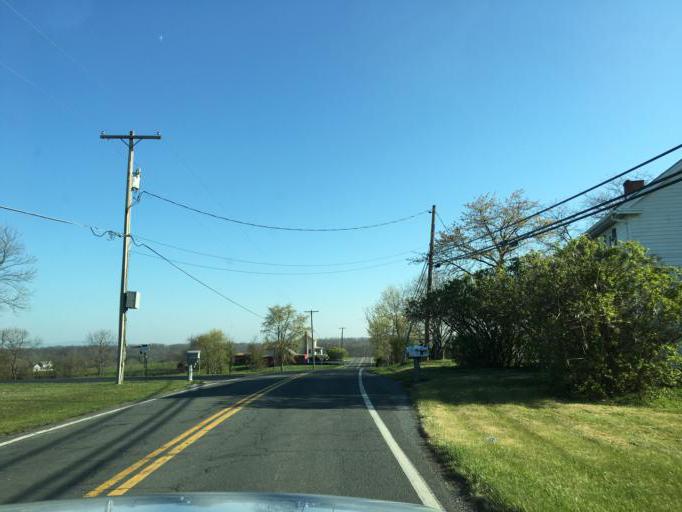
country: US
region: Maryland
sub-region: Frederick County
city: Woodsboro
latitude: 39.4888
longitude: -77.2947
